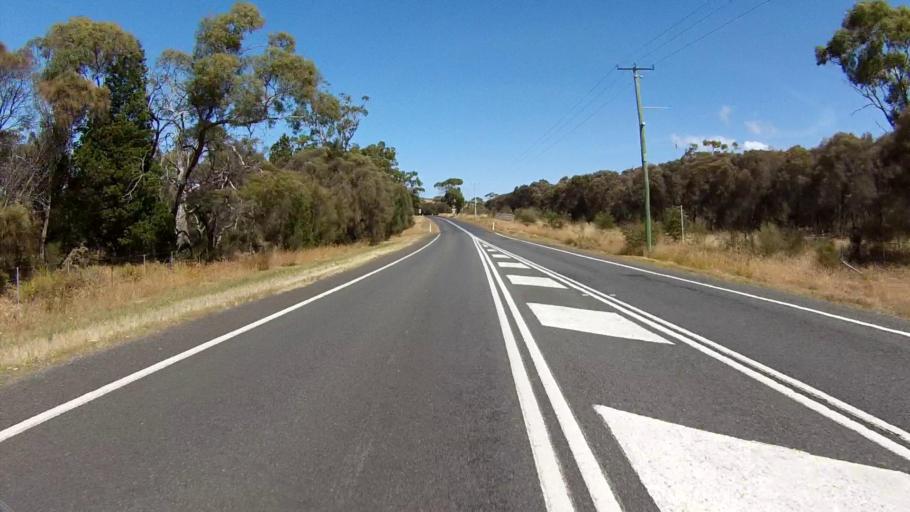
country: AU
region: Tasmania
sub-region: Sorell
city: Sorell
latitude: -42.1435
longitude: 148.0684
